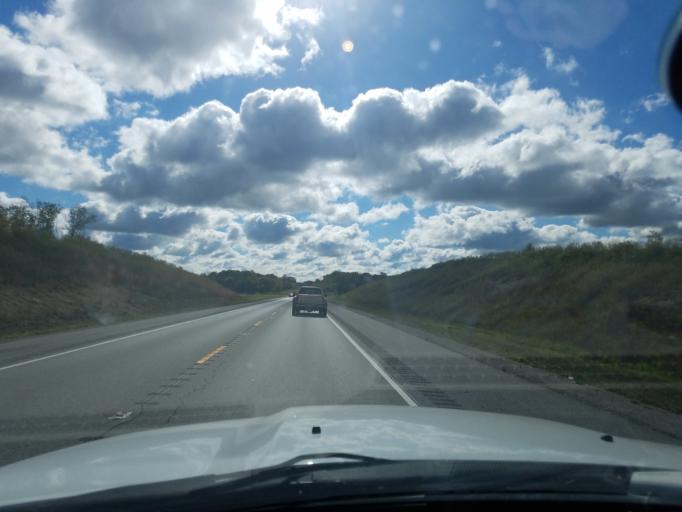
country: US
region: Kentucky
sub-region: Rockcastle County
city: Brodhead
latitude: 37.4284
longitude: -84.4564
